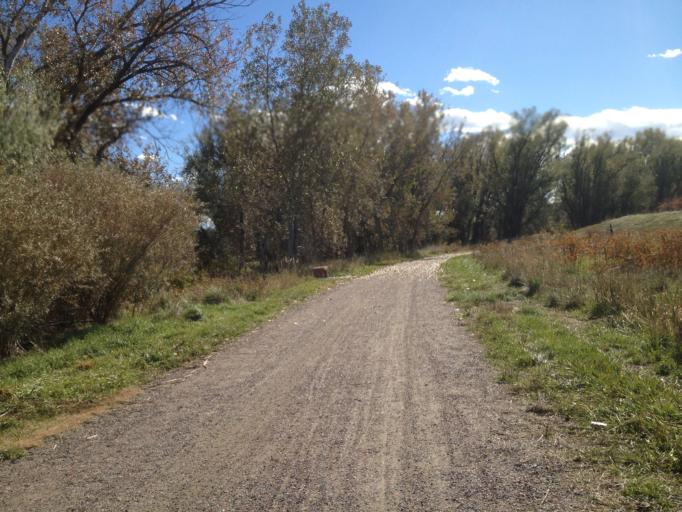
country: US
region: Colorado
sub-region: Boulder County
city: Superior
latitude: 39.9570
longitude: -105.1563
